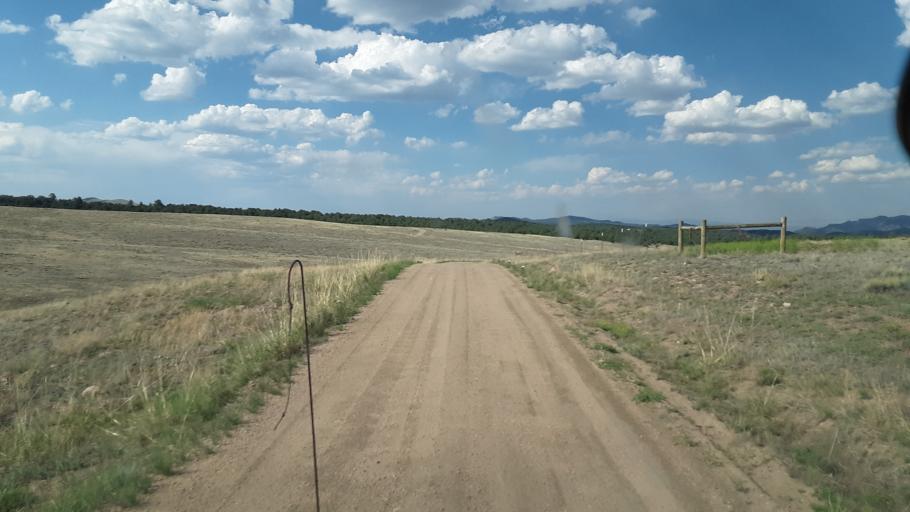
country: US
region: Colorado
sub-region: Custer County
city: Westcliffe
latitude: 38.2683
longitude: -105.4769
